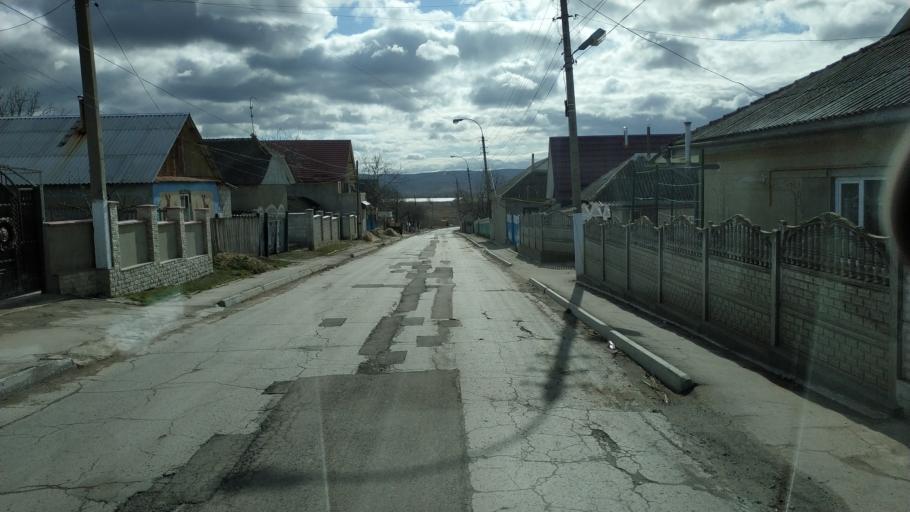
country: MD
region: Stinga Nistrului
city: Bucovat
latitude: 47.2067
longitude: 28.4966
